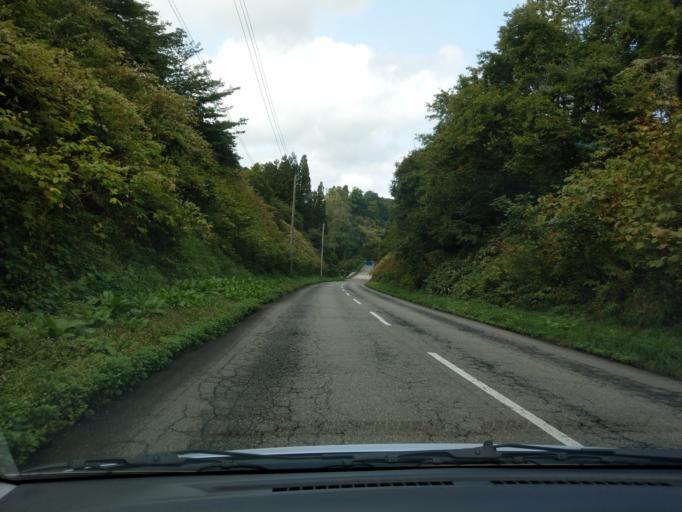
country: JP
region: Akita
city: Omagari
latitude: 39.4726
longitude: 140.3124
